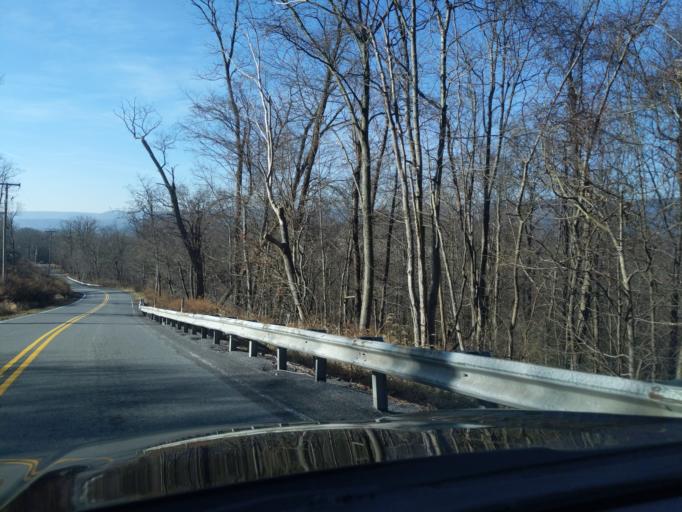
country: US
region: Pennsylvania
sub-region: Blair County
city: Tipton
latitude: 40.6176
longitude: -78.2941
